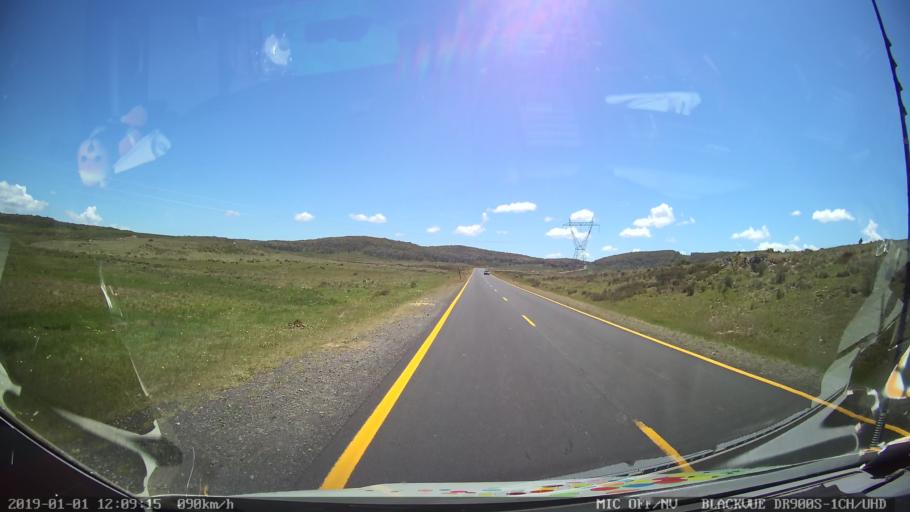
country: AU
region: New South Wales
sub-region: Tumut Shire
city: Tumut
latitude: -35.8096
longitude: 148.4961
